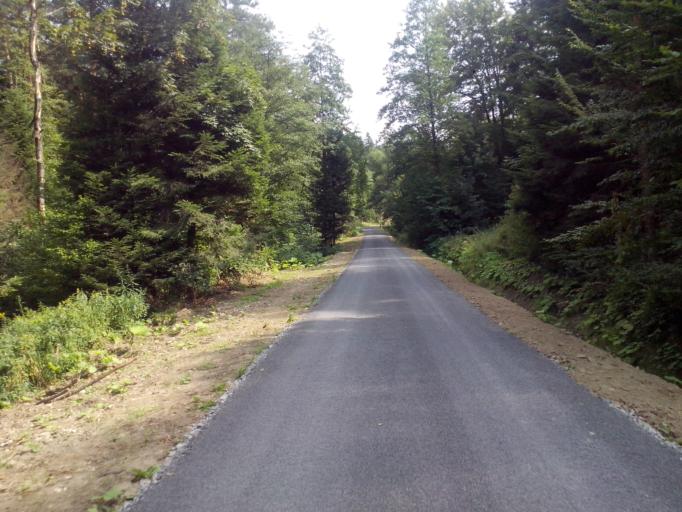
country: PL
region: Subcarpathian Voivodeship
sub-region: Powiat strzyzowski
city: Strzyzow
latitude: 49.8039
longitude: 21.8119
